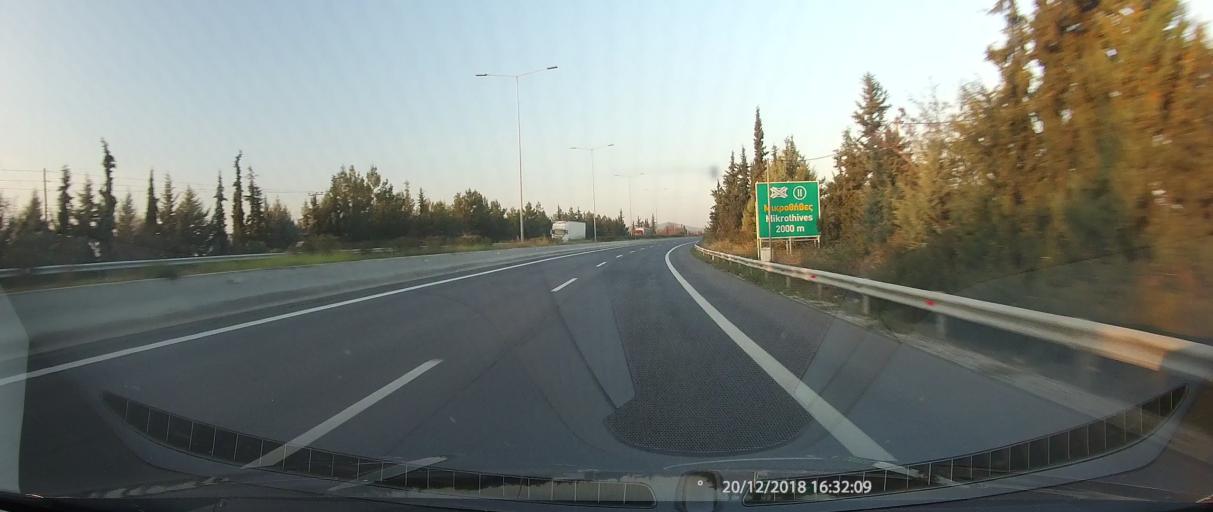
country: GR
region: Thessaly
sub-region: Nomos Magnisias
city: Evxinoupolis
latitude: 39.2393
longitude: 22.7339
